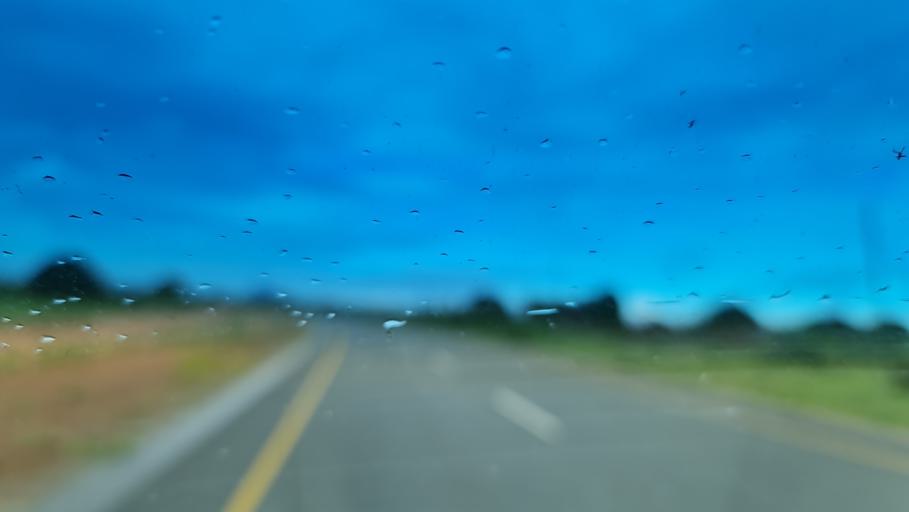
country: MZ
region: Nampula
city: Nampula
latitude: -15.5480
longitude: 39.3231
